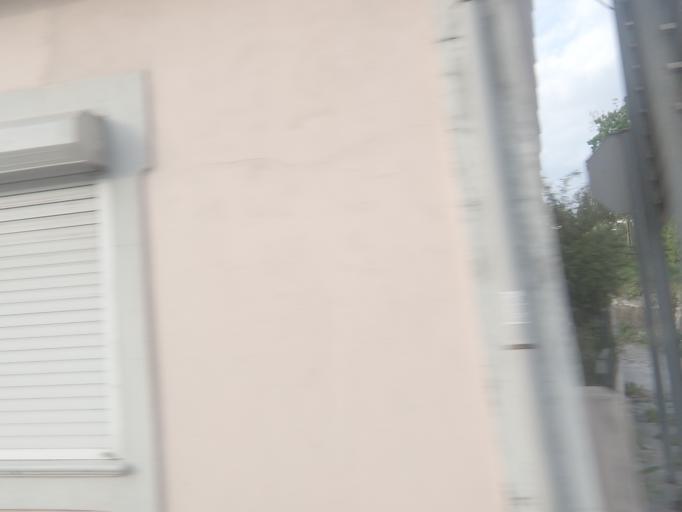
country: PT
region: Porto
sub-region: Valongo
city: Campo
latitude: 41.1831
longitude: -8.4692
